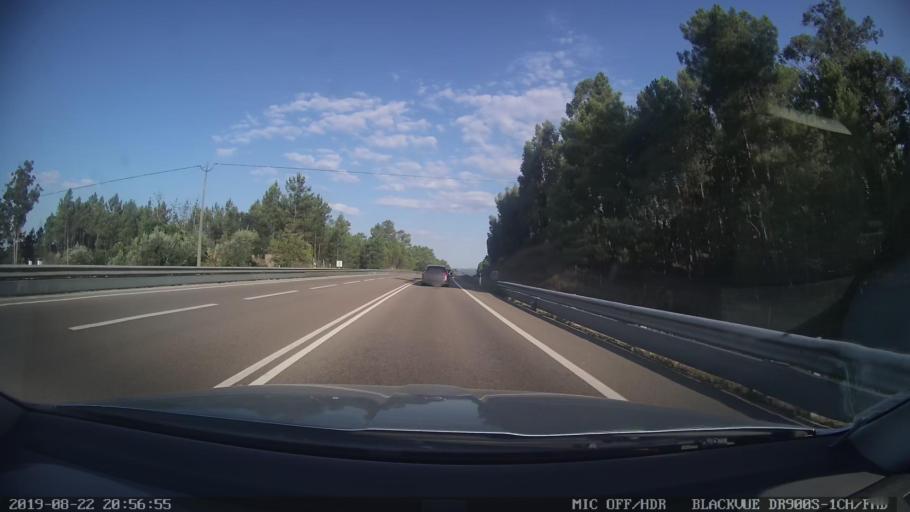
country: PT
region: Castelo Branco
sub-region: Serta
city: Serta
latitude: 39.7905
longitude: -8.0574
